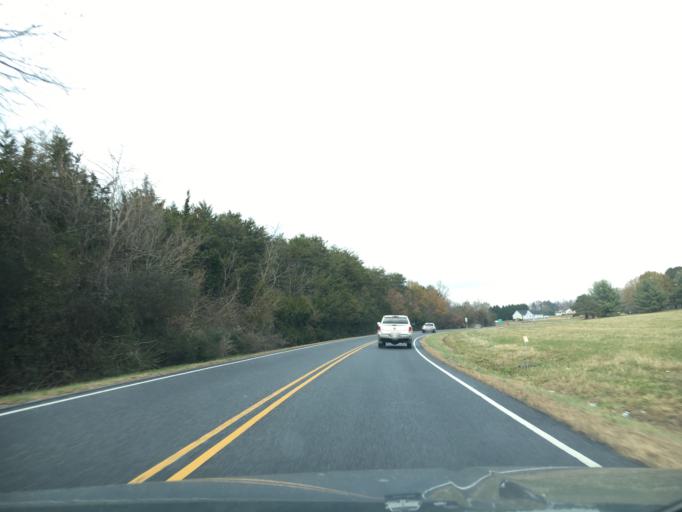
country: US
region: Virginia
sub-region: Prince Edward County
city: Farmville
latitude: 37.3383
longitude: -78.3897
